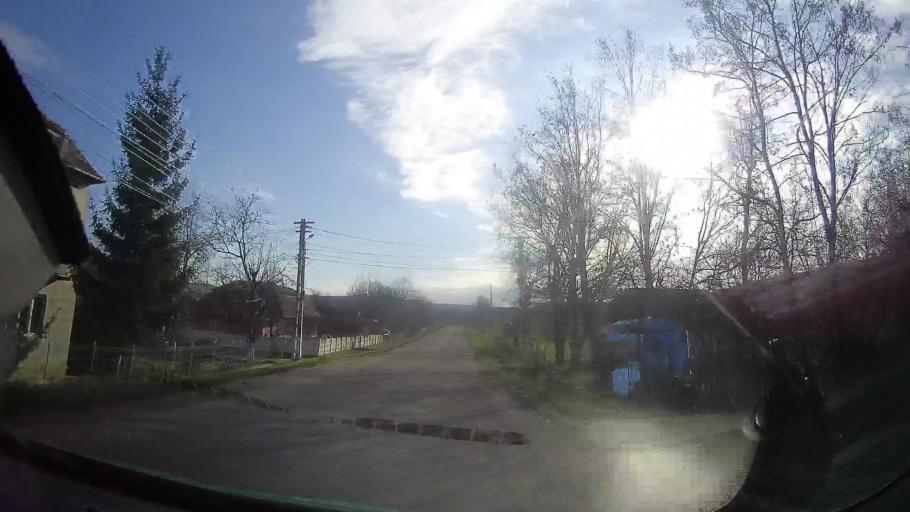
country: RO
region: Mures
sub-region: Comuna Valea Larga
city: Valea Larga
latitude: 46.6082
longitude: 24.0915
